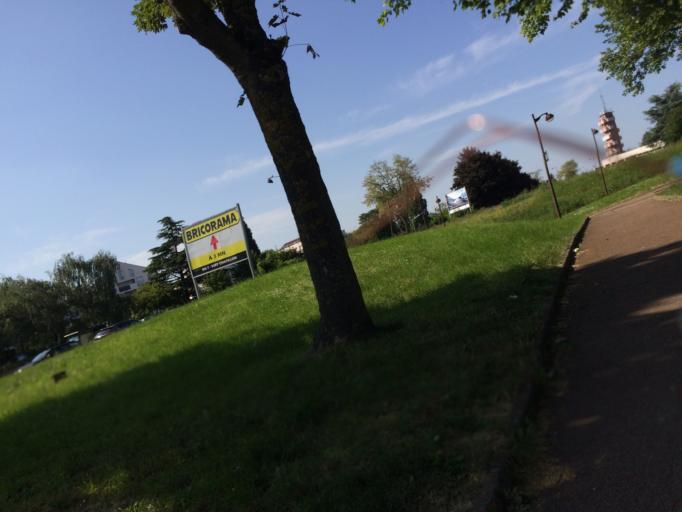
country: FR
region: Ile-de-France
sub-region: Departement de l'Essonne
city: Morsang-sur-Orge
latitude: 48.6563
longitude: 2.3724
